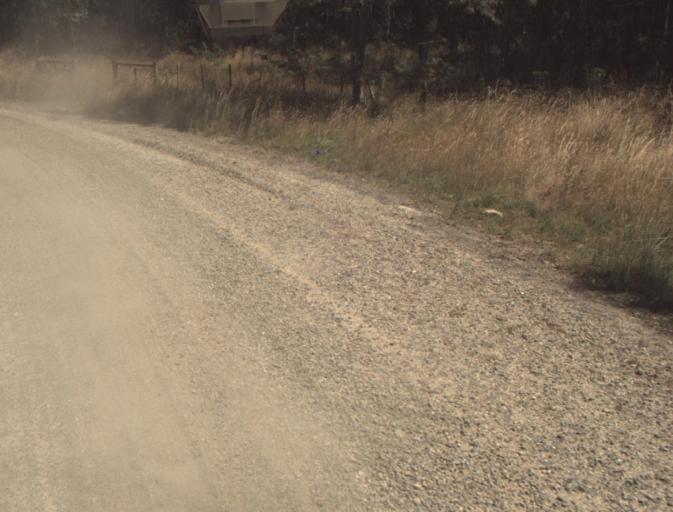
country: AU
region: Tasmania
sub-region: Dorset
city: Scottsdale
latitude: -41.3286
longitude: 147.4426
